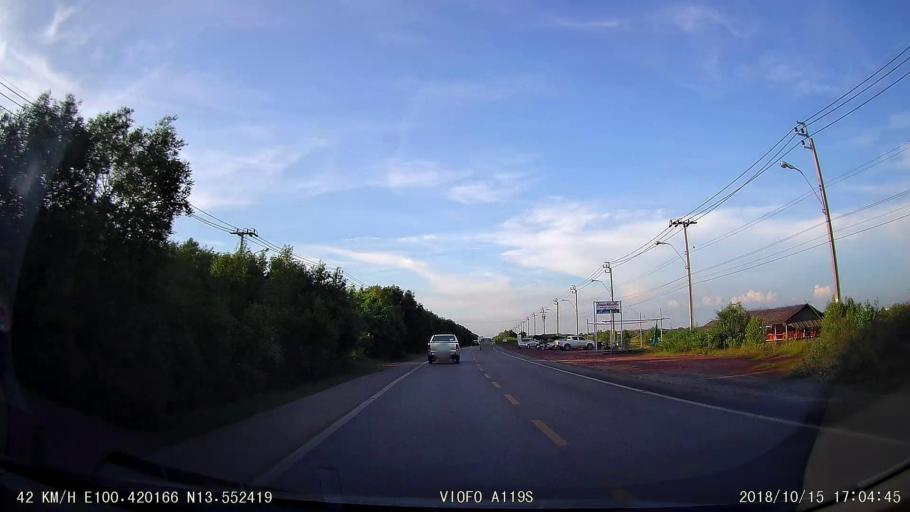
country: TH
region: Bangkok
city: Bang Khun Thian
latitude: 13.5526
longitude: 100.4201
